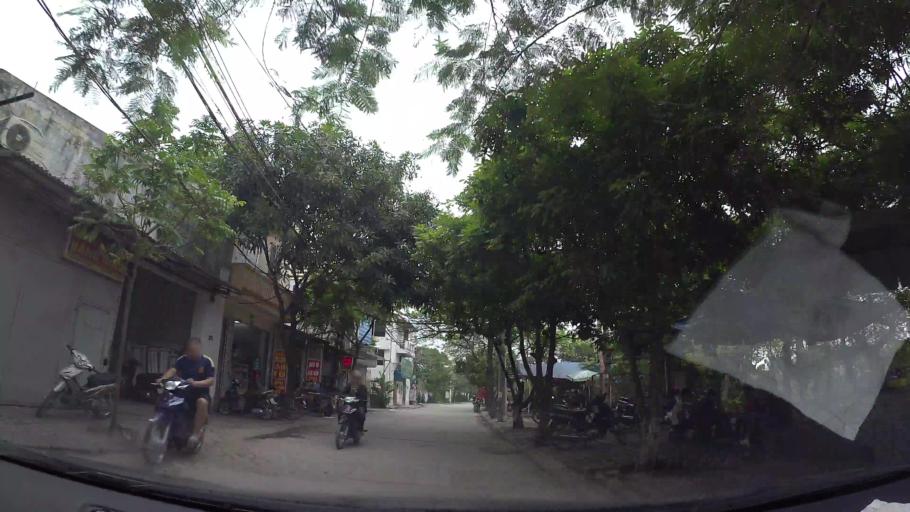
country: VN
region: Ha Noi
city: Hai BaTrung
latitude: 20.9962
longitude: 105.8829
